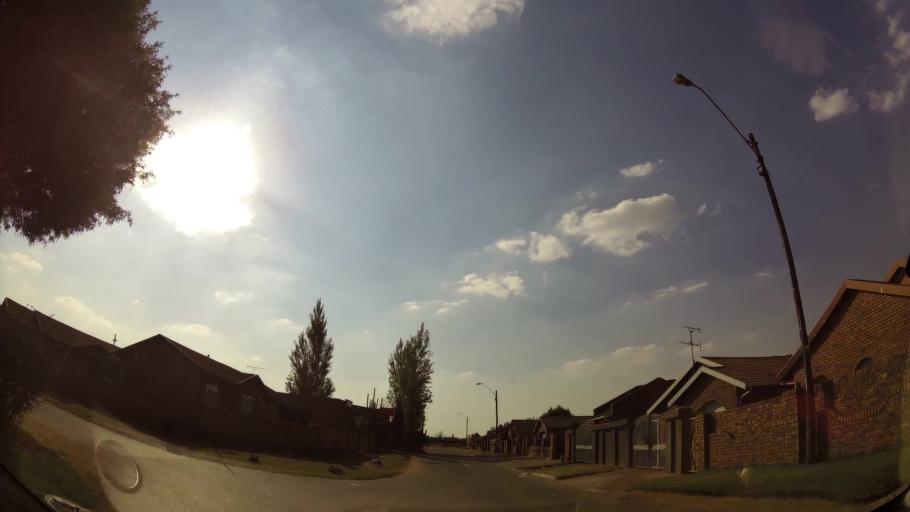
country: ZA
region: Gauteng
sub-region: Ekurhuleni Metropolitan Municipality
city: Benoni
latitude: -26.1521
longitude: 28.4002
